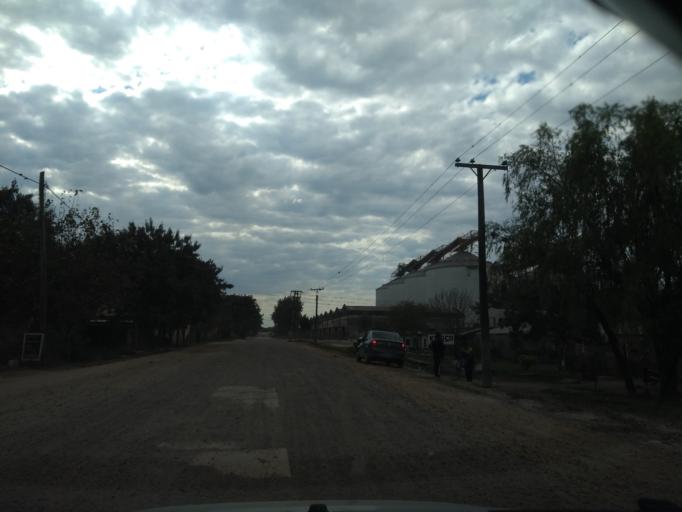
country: AR
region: Chaco
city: Puerto Vilelas
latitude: -27.5347
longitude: -58.9228
